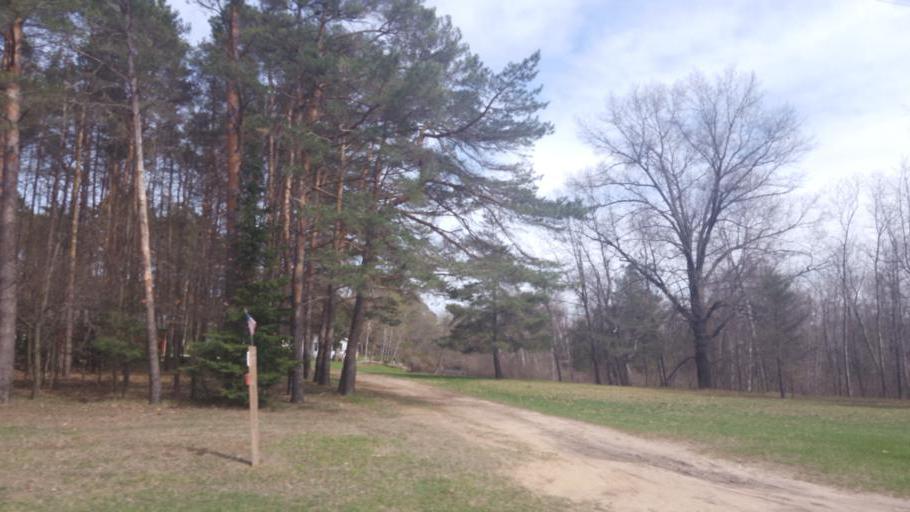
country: US
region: Michigan
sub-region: Gladwin County
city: Gladwin
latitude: 44.0062
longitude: -84.5254
